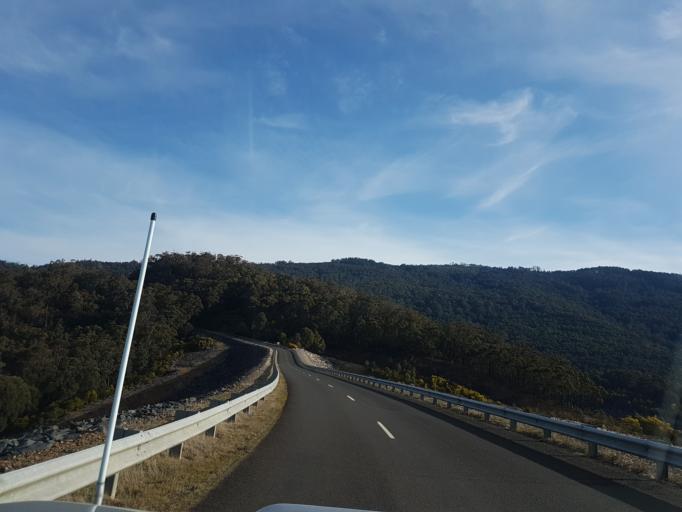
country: AU
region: Victoria
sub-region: Latrobe
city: Moe
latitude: -37.8456
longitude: 146.3954
